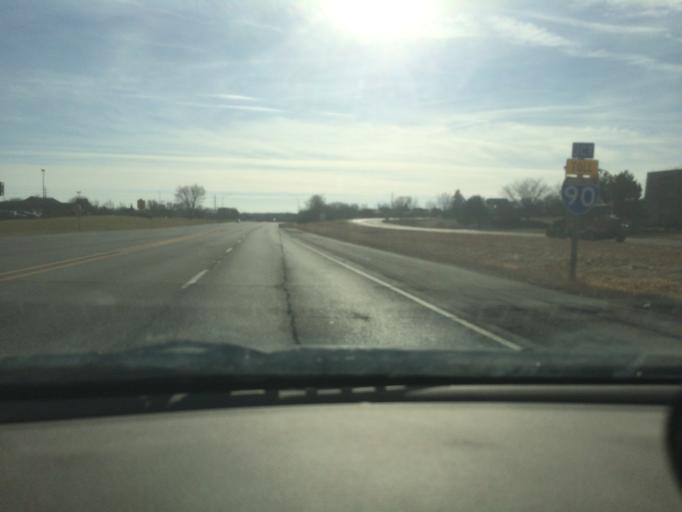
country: US
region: Illinois
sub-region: Kane County
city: Sleepy Hollow
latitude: 42.0733
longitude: -88.2904
